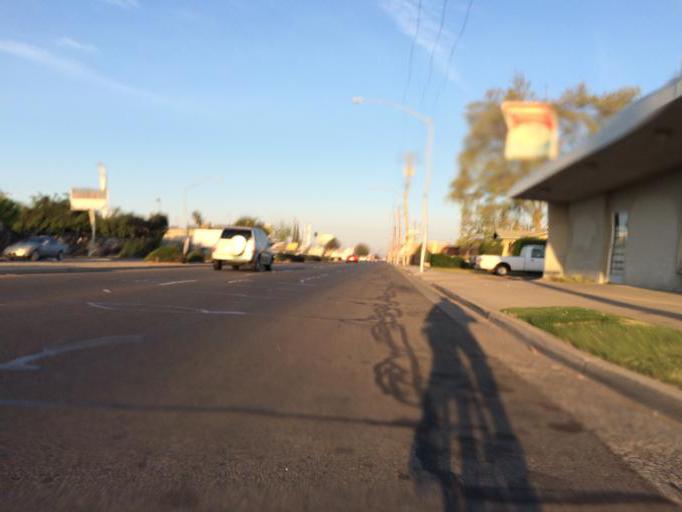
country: US
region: California
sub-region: Fresno County
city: Fresno
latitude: 36.7505
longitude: -119.7411
